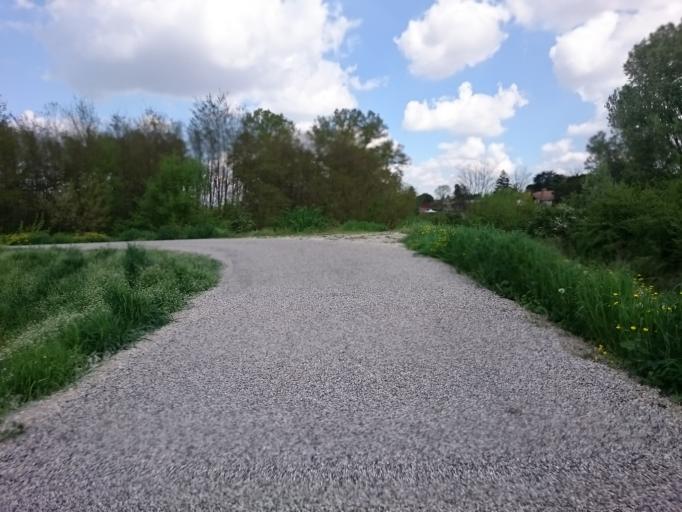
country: IT
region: Veneto
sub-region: Provincia di Padova
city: Tencarola
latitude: 45.3891
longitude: 11.8286
